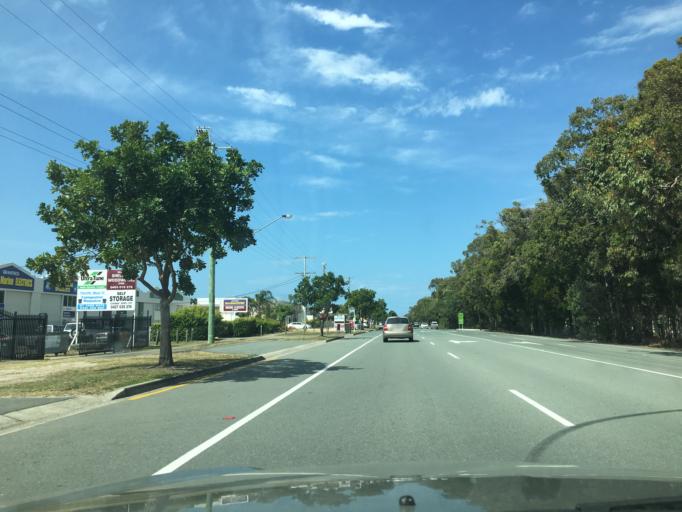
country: AU
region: Queensland
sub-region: Moreton Bay
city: Bongaree
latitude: -27.0796
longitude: 153.1764
